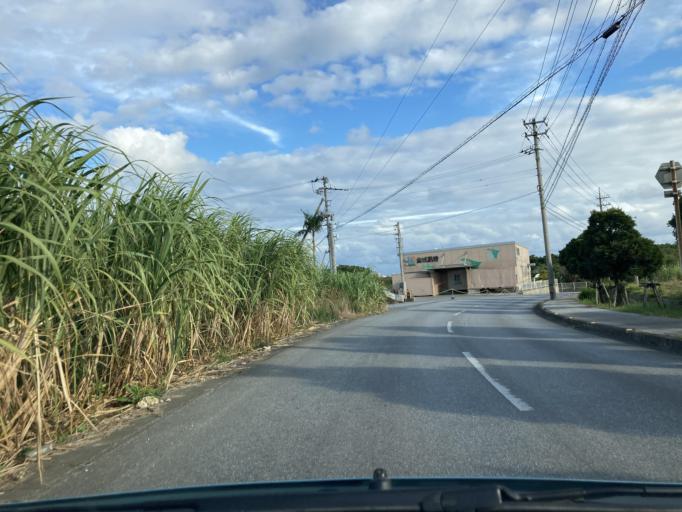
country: JP
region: Okinawa
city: Itoman
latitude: 26.1351
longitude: 127.7494
